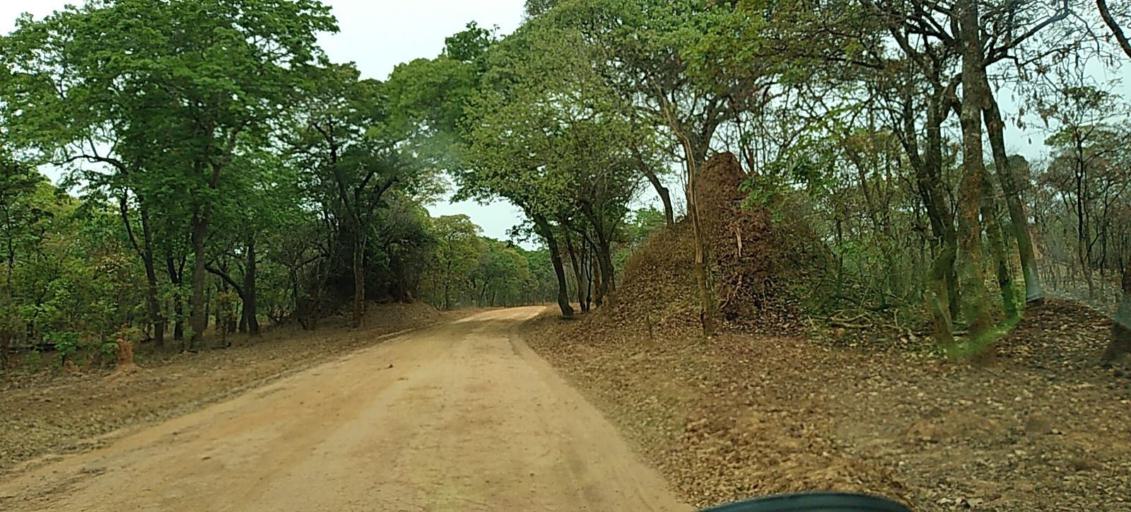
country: ZM
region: North-Western
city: Solwezi
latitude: -12.9141
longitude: 26.5568
